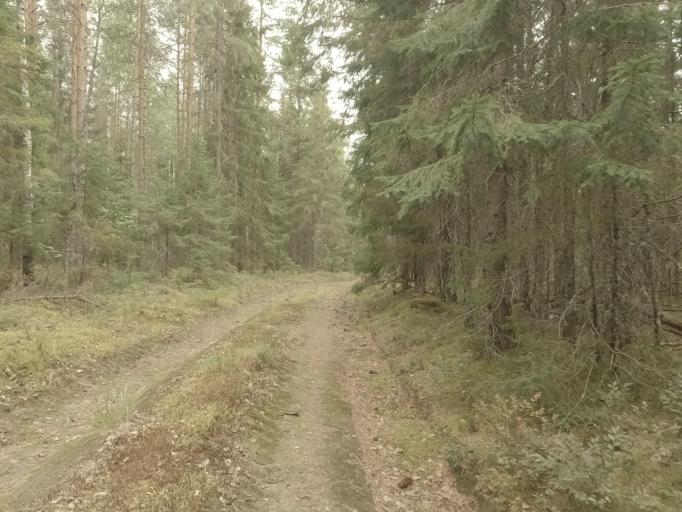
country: RU
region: Leningrad
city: Kamennogorsk
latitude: 61.0427
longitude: 29.1865
